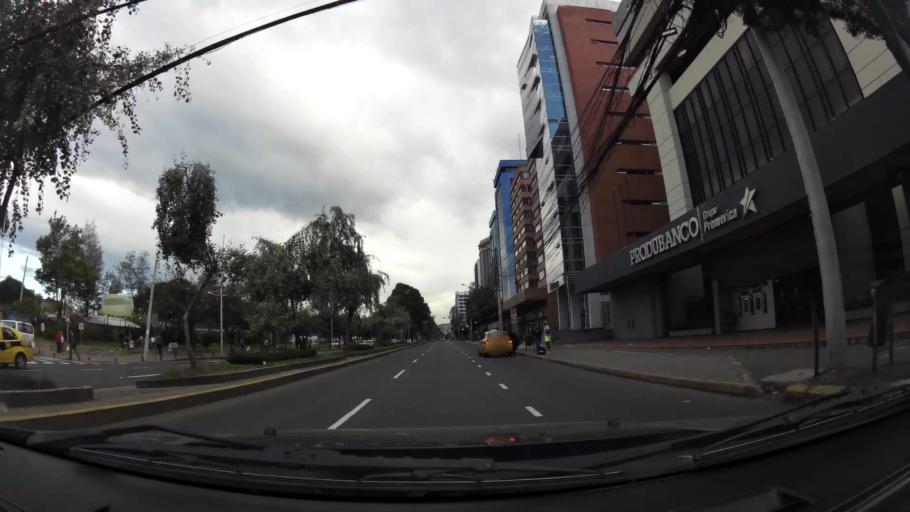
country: EC
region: Pichincha
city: Quito
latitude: -0.1785
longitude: -78.4861
